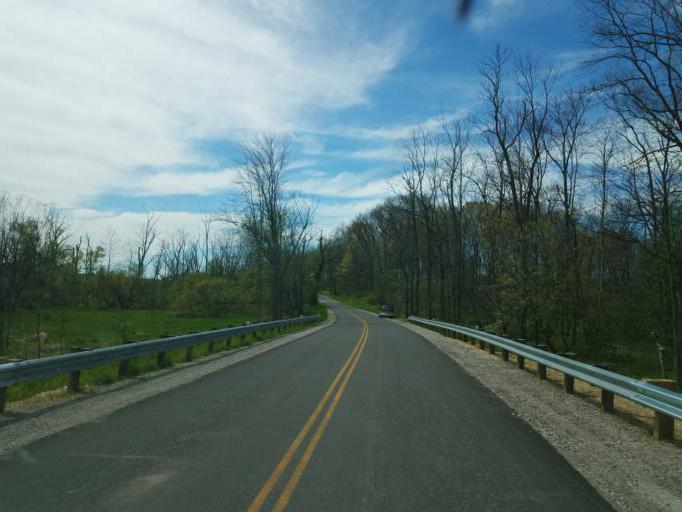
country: US
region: Ohio
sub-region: Huron County
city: Greenwich
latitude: 40.9011
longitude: -82.5273
